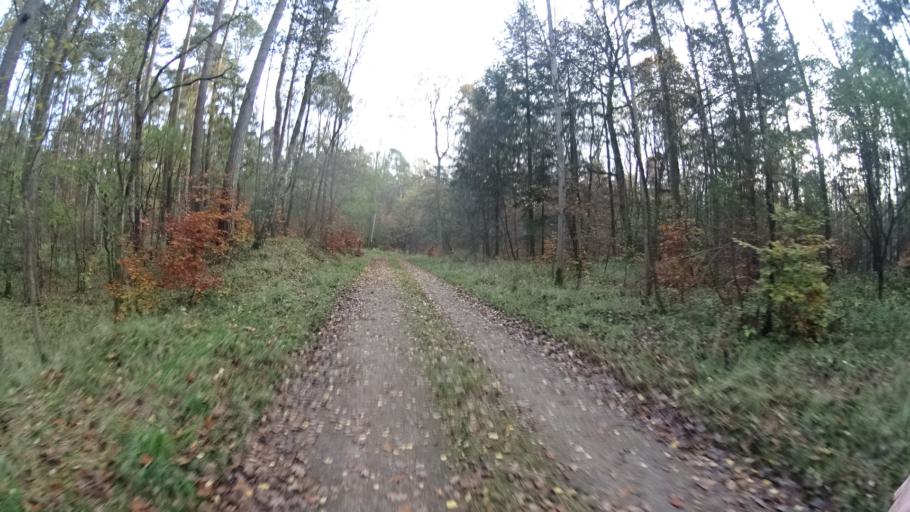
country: DE
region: Lower Saxony
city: Deutsch Evern
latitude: 53.2250
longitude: 10.4304
